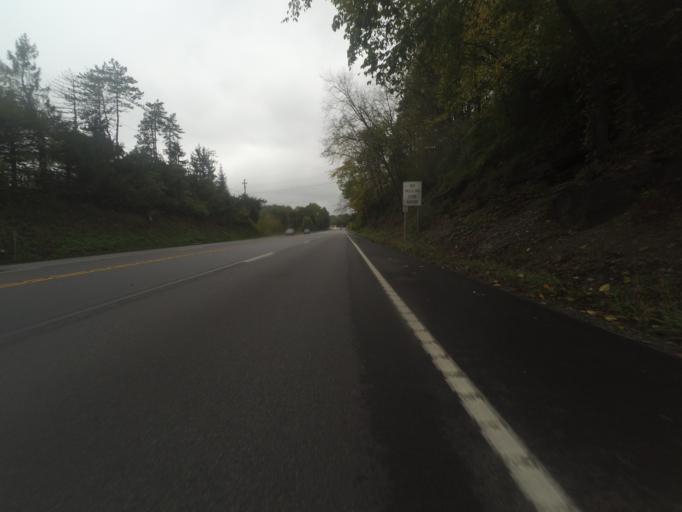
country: US
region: Pennsylvania
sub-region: Huntingdon County
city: McConnellstown
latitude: 40.5338
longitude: -78.0853
